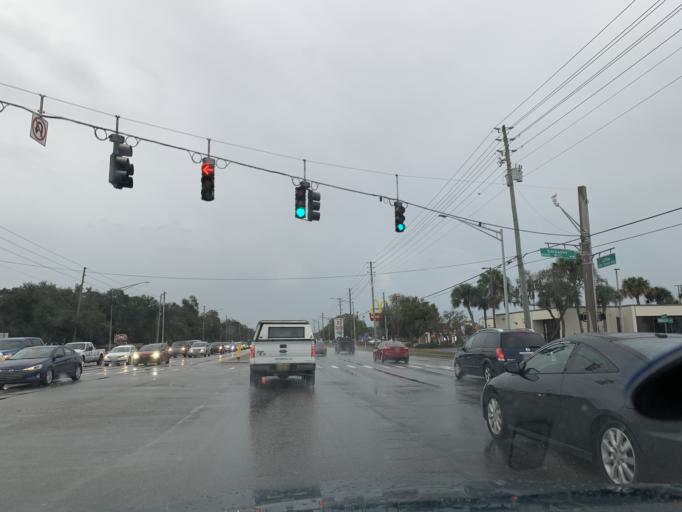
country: US
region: Florida
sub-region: Pasco County
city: Jasmine Estates
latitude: 28.2918
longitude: -82.6759
